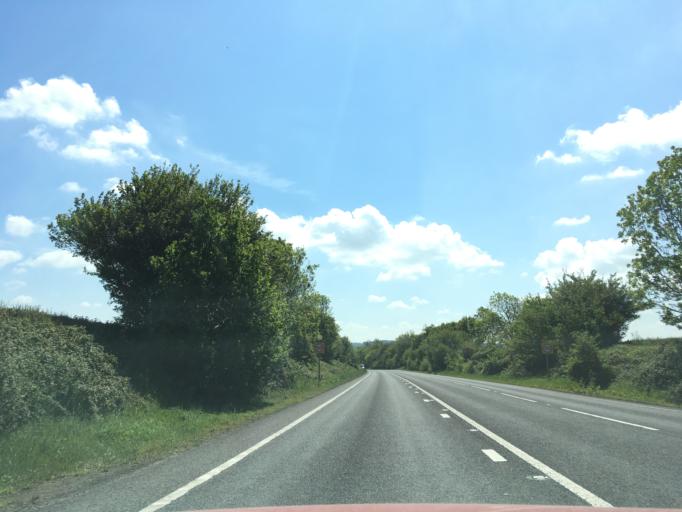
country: GB
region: England
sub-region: Oxfordshire
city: Banbury
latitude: 52.0713
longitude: -1.2855
